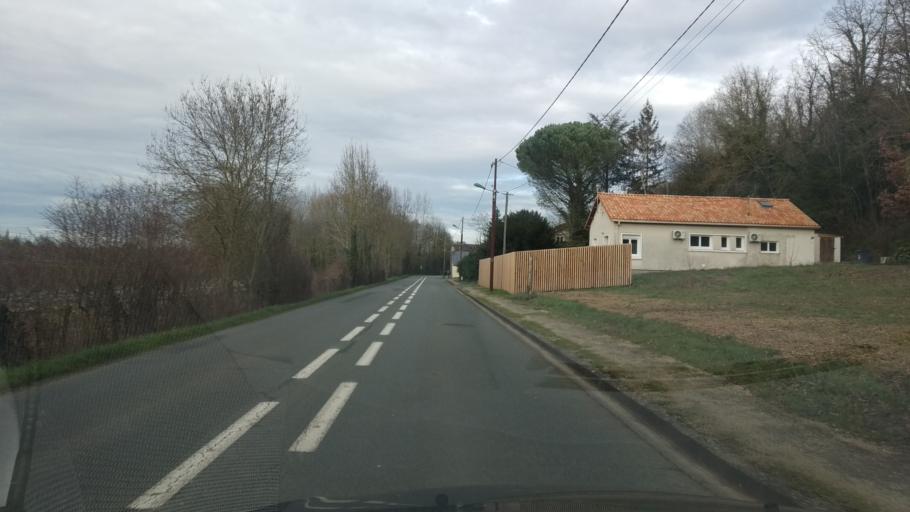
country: FR
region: Poitou-Charentes
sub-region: Departement de la Vienne
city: Chasseneuil-du-Poitou
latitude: 46.6433
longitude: 0.3798
